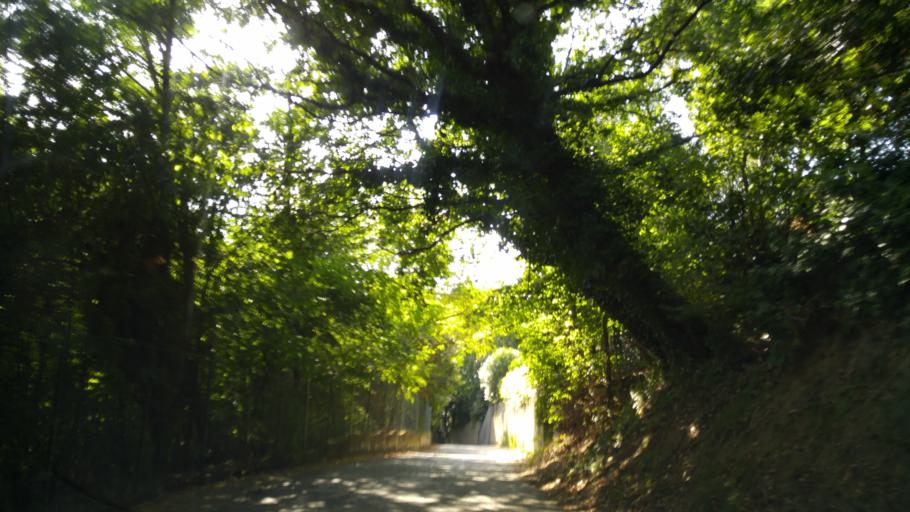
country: IT
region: The Marches
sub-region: Provincia di Pesaro e Urbino
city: Pesaro
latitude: 43.8977
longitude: 12.9294
